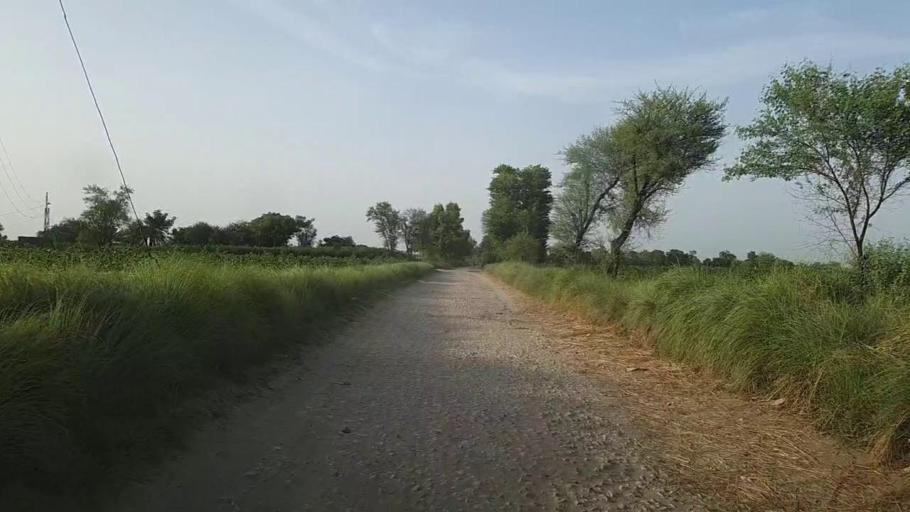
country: PK
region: Sindh
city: Bhiria
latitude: 26.8931
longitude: 68.2619
